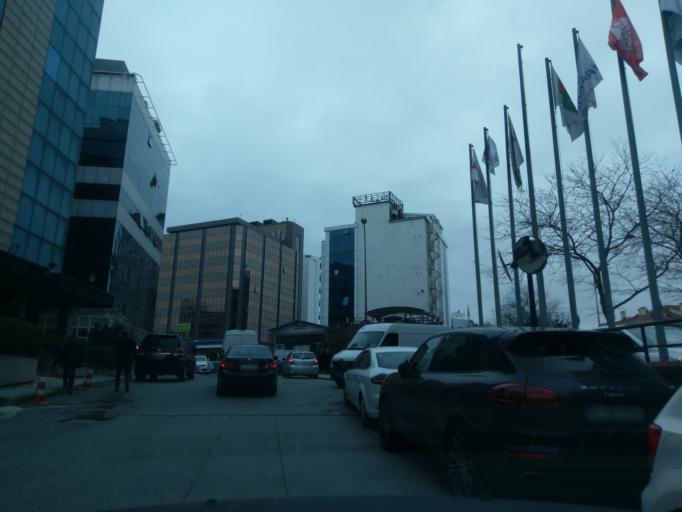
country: TR
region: Istanbul
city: Umraniye
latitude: 41.0925
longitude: 29.0962
